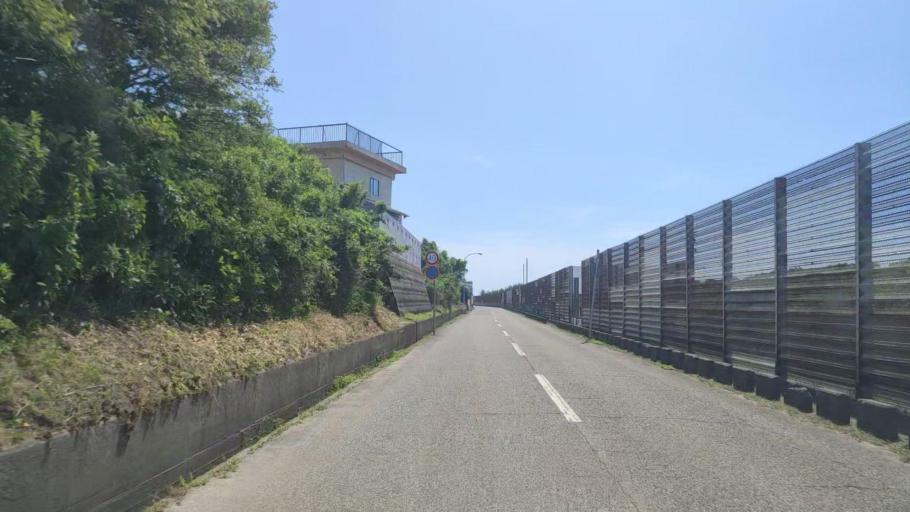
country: JP
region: Ishikawa
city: Kanazawa-shi
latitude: 36.6075
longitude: 136.5935
